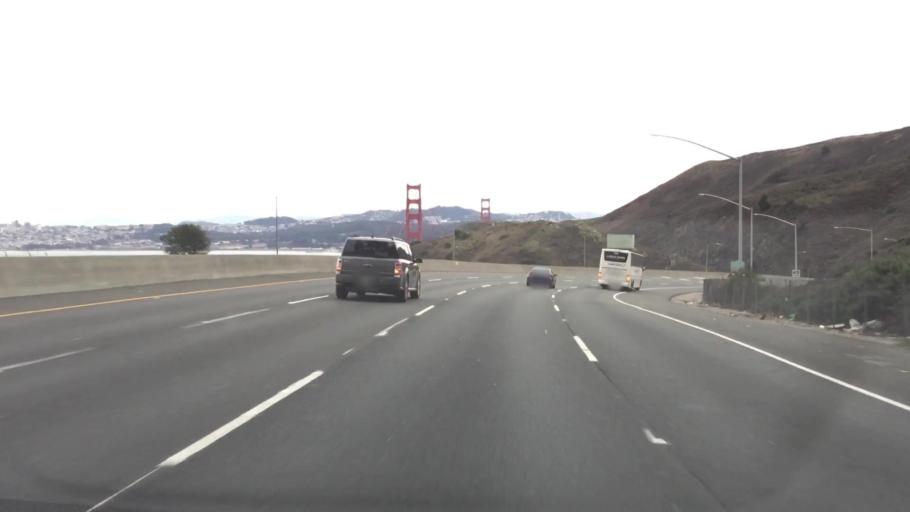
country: US
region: California
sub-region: Marin County
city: Sausalito
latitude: 37.8431
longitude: -122.4860
